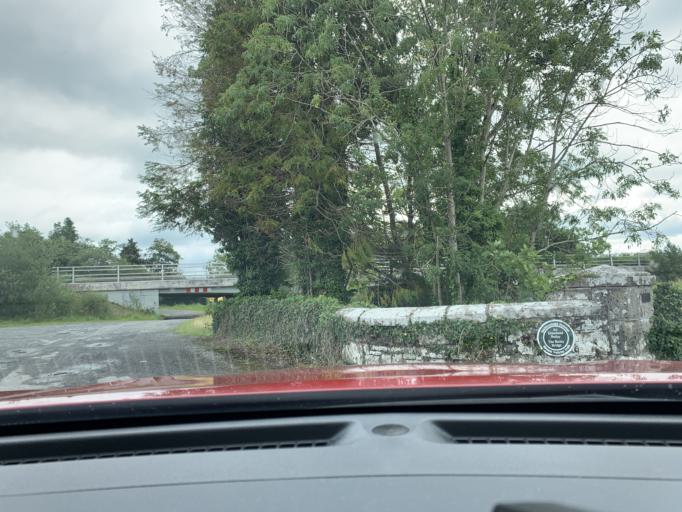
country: IE
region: Connaught
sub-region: Roscommon
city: Boyle
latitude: 53.9848
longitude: -8.2810
